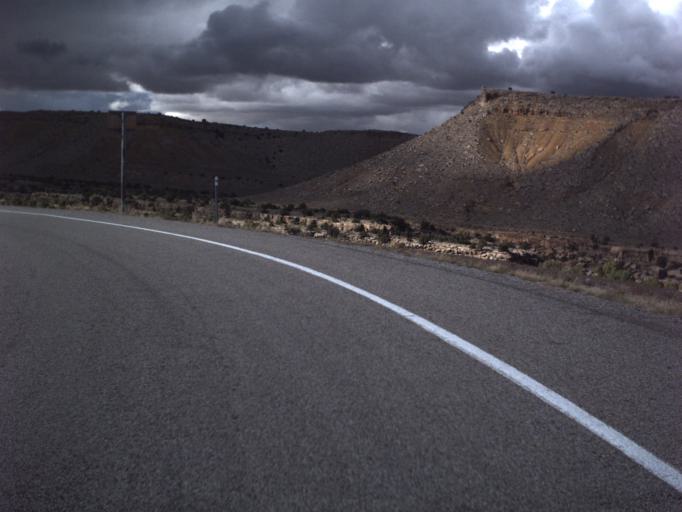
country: US
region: Utah
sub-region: Emery County
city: Castle Dale
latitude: 38.9396
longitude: -110.4811
